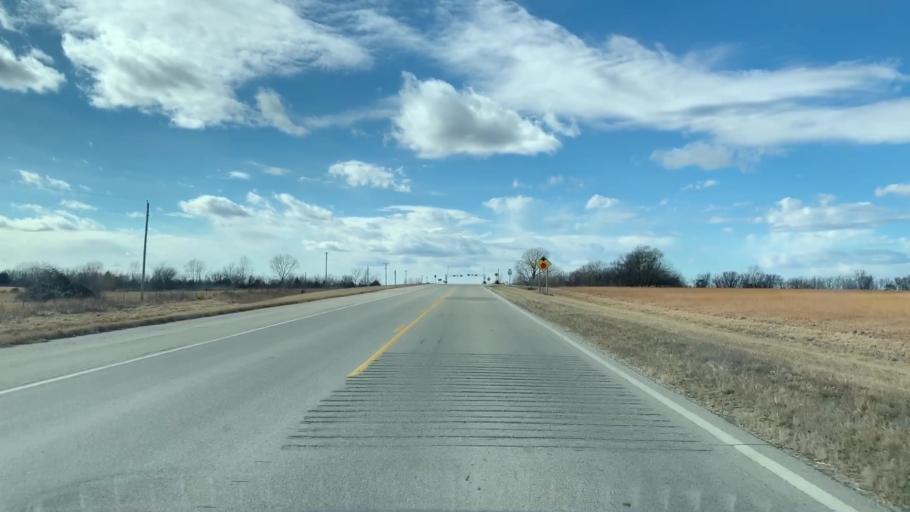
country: US
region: Kansas
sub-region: Neosho County
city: Chanute
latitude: 37.5288
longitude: -95.4659
